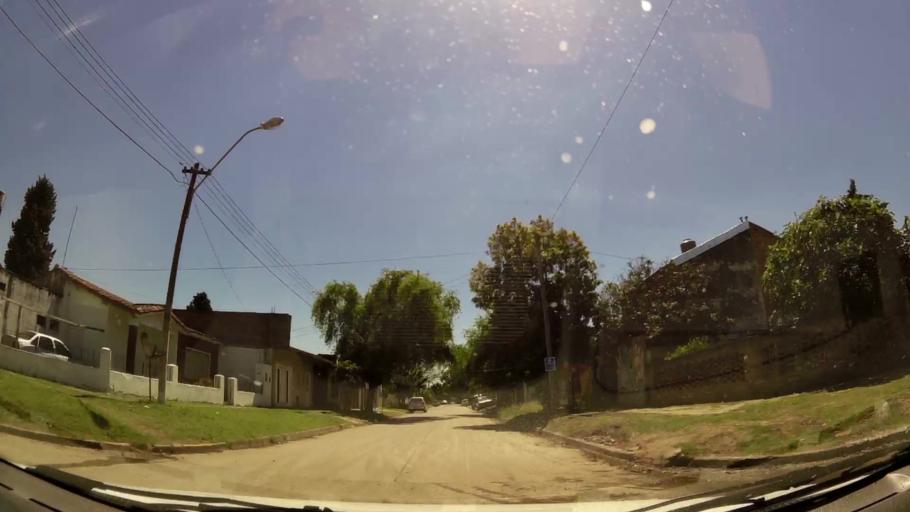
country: AR
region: Buenos Aires
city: Ituzaingo
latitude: -34.6773
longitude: -58.6738
